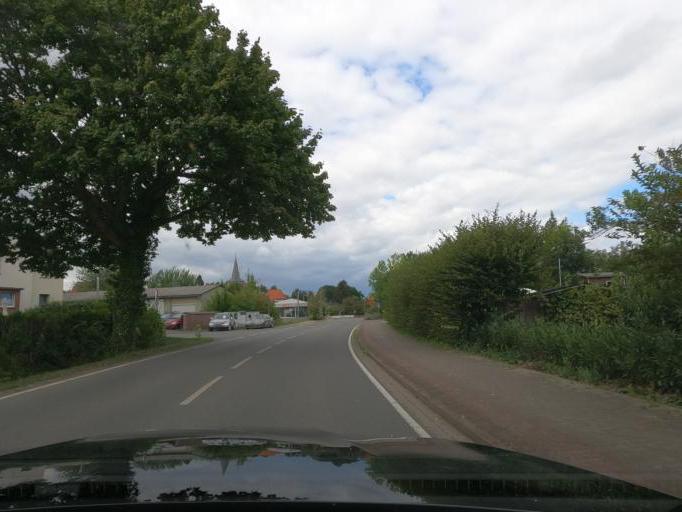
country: DE
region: Lower Saxony
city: Algermissen
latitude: 52.2699
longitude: 9.9527
